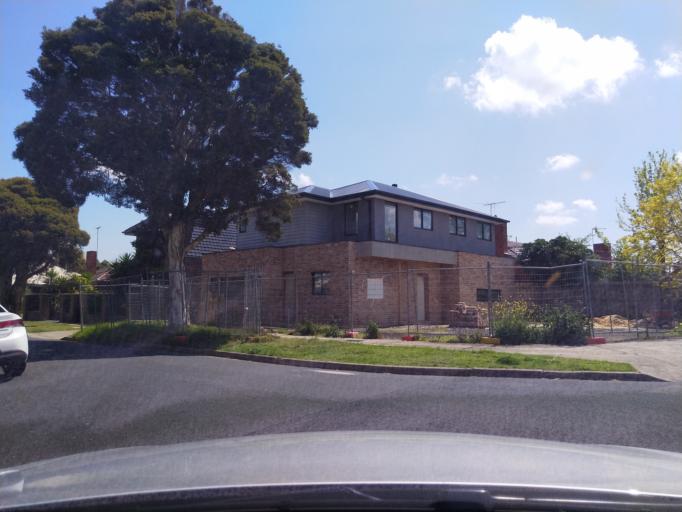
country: AU
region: Victoria
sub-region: Banyule
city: Bellfield
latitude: -37.7531
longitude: 145.0436
